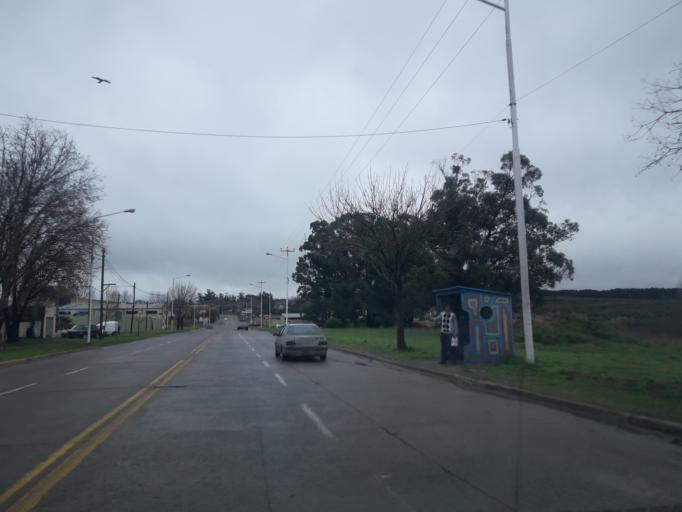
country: AR
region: Buenos Aires
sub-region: Partido de Tandil
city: Tandil
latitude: -37.3216
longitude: -59.1658
